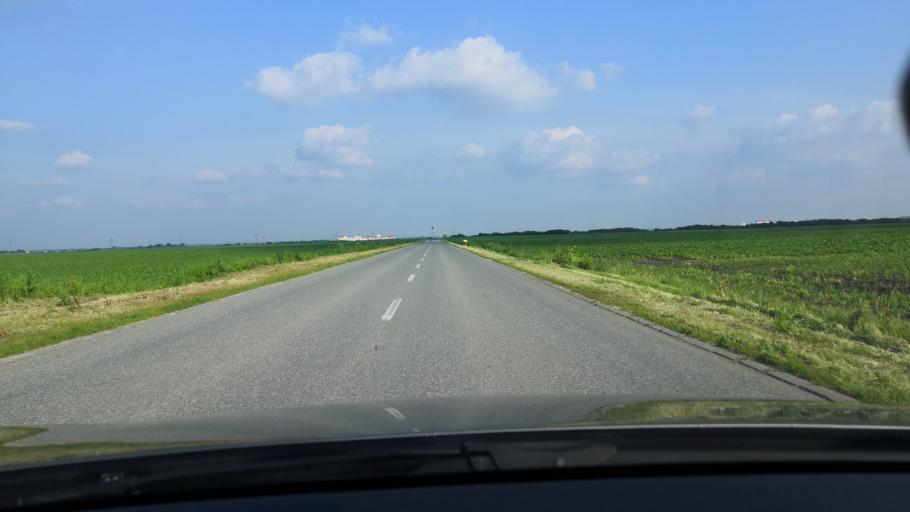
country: RS
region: Autonomna Pokrajina Vojvodina
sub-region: Sremski Okrug
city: Ingija
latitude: 45.0810
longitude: 20.1175
